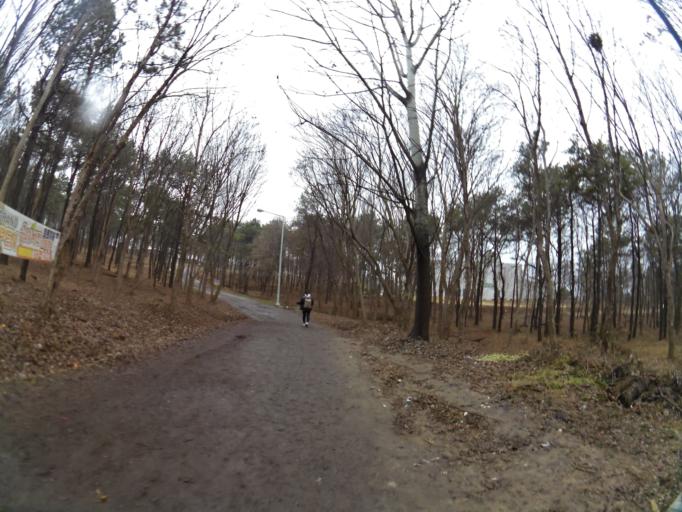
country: KR
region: Gyeongsangbuk-do
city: Gyeongsan-si
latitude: 35.8371
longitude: 128.7577
